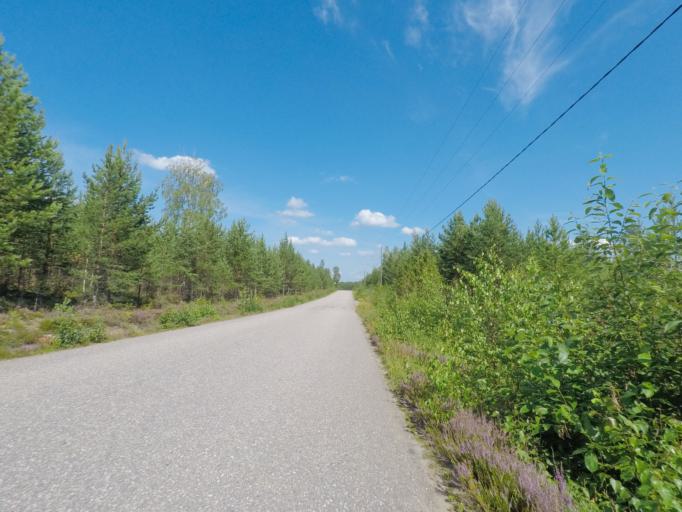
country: FI
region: Southern Savonia
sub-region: Mikkeli
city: Puumala
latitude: 61.4279
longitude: 28.1630
